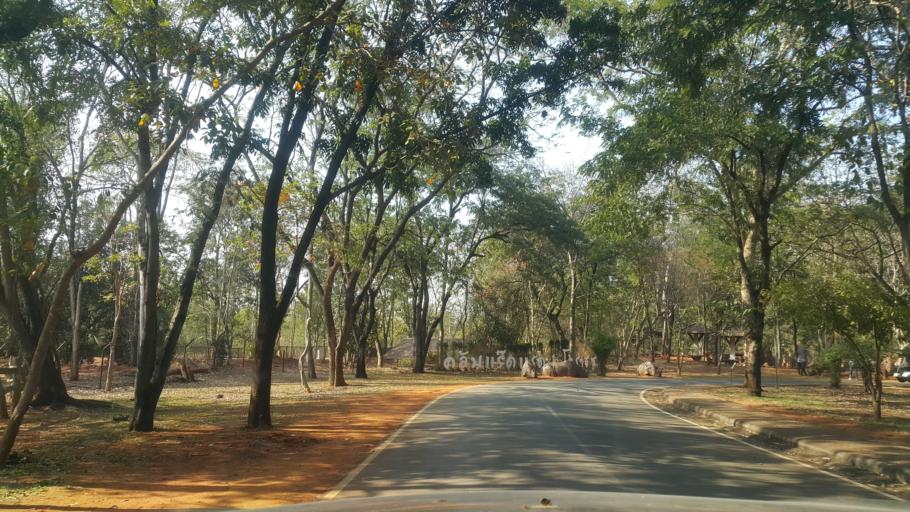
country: TH
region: Nakhon Ratchasima
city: Nakhon Ratchasima
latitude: 14.8539
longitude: 102.0863
